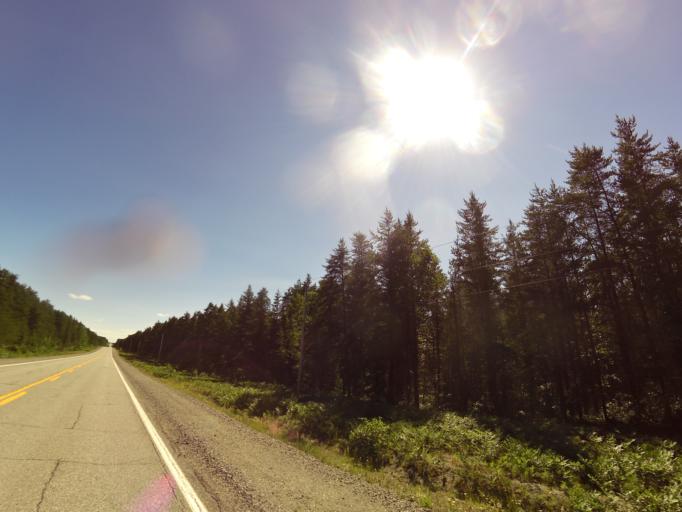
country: CA
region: Quebec
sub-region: Abitibi-Temiscamingue
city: Senneterre
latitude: 48.1281
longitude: -77.3813
